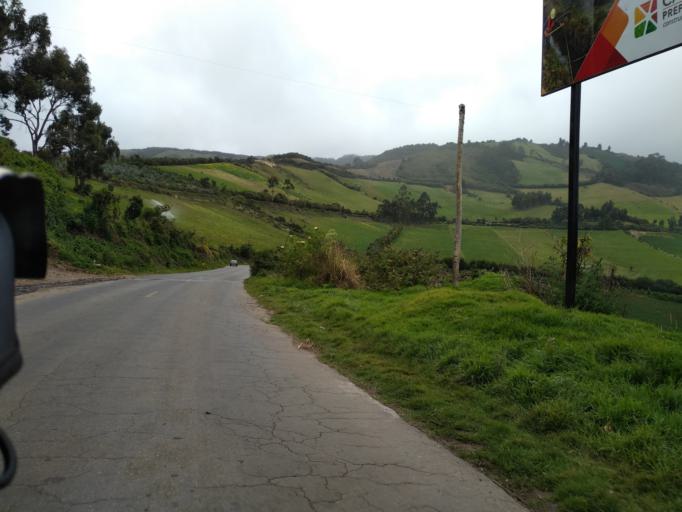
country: EC
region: Carchi
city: El Angel
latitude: 0.6333
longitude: -77.9332
